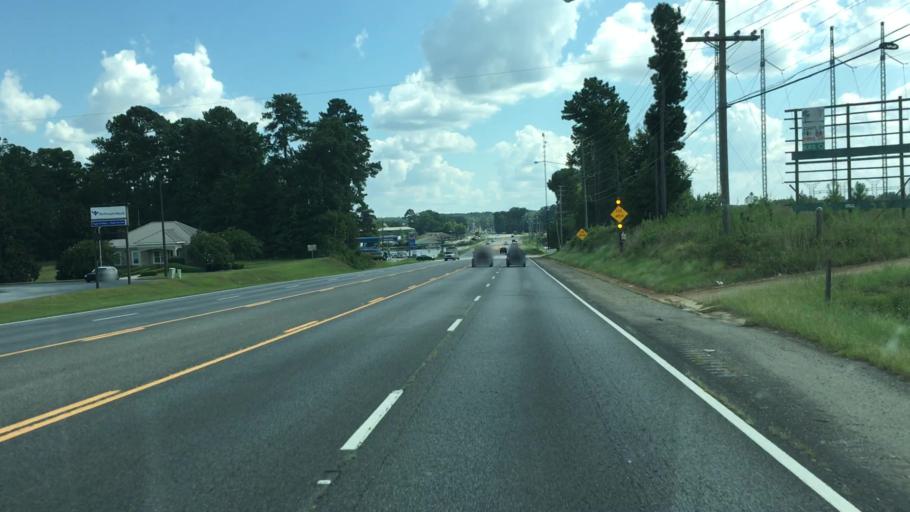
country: US
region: Georgia
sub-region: Baldwin County
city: Milledgeville
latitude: 33.2008
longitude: -83.2956
